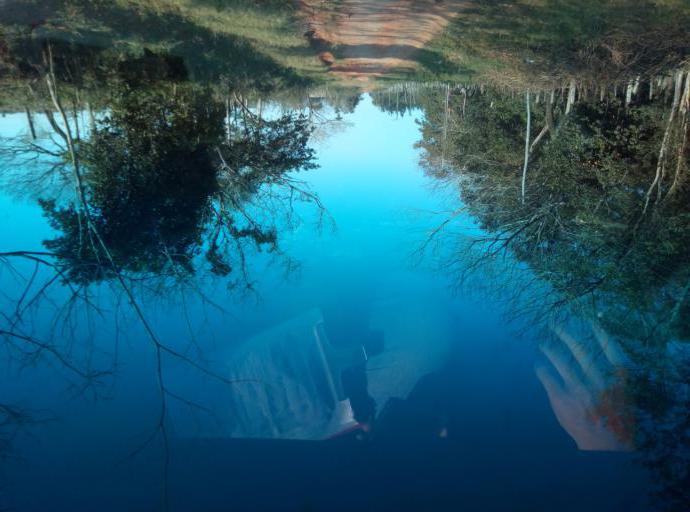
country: PY
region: Caaguazu
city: Doctor Cecilio Baez
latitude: -25.1665
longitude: -56.2320
